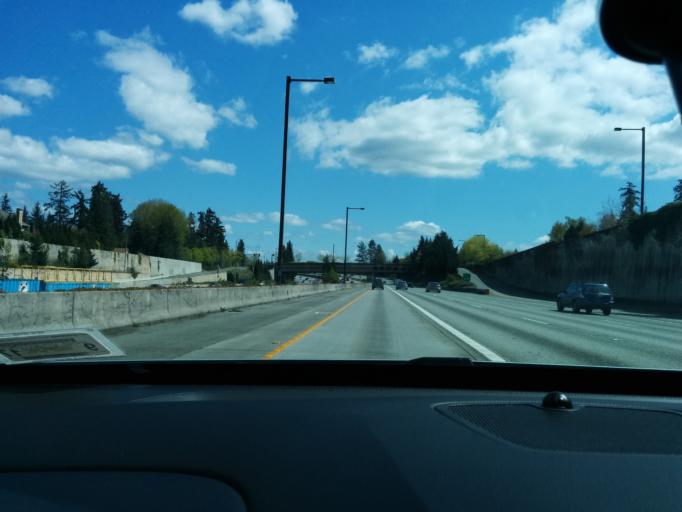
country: US
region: Washington
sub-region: King County
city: Mercer Island
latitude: 47.5784
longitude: -122.2121
